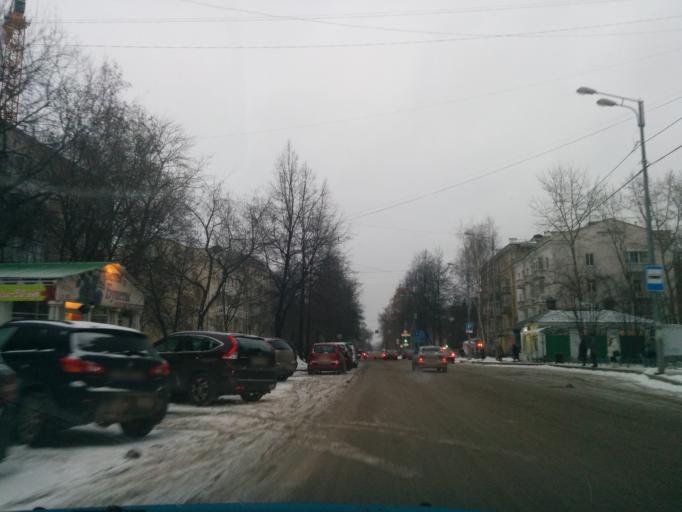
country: RU
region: Perm
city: Perm
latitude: 58.0103
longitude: 56.2503
